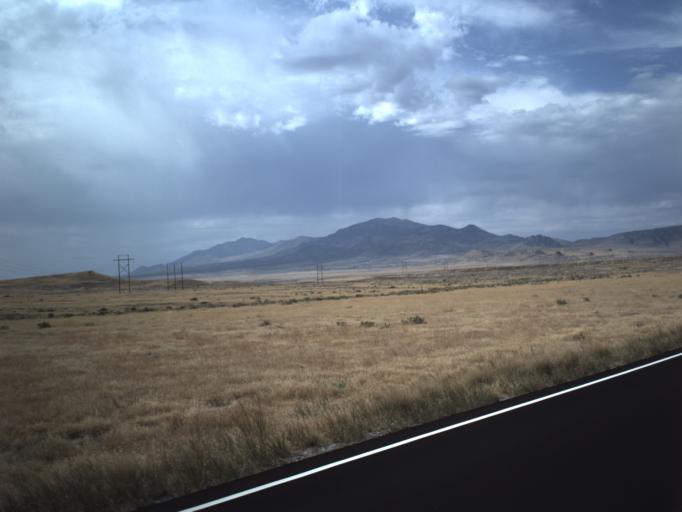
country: US
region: Utah
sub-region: Tooele County
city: Wendover
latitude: 41.4131
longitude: -113.9233
